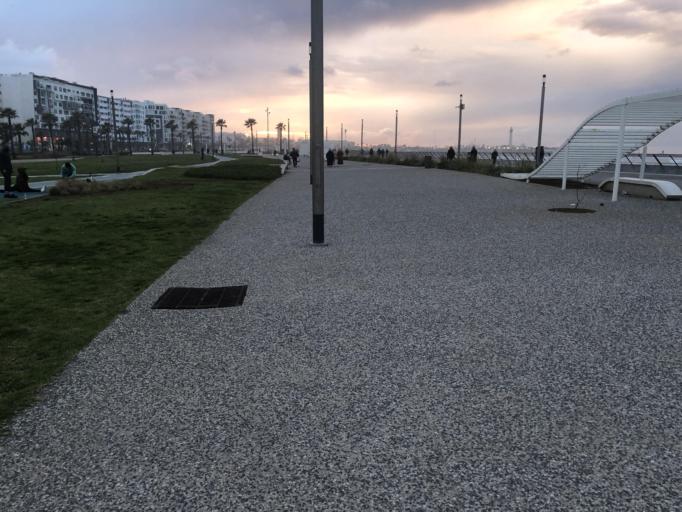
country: MA
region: Grand Casablanca
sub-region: Casablanca
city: Casablanca
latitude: 33.6045
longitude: -7.6407
